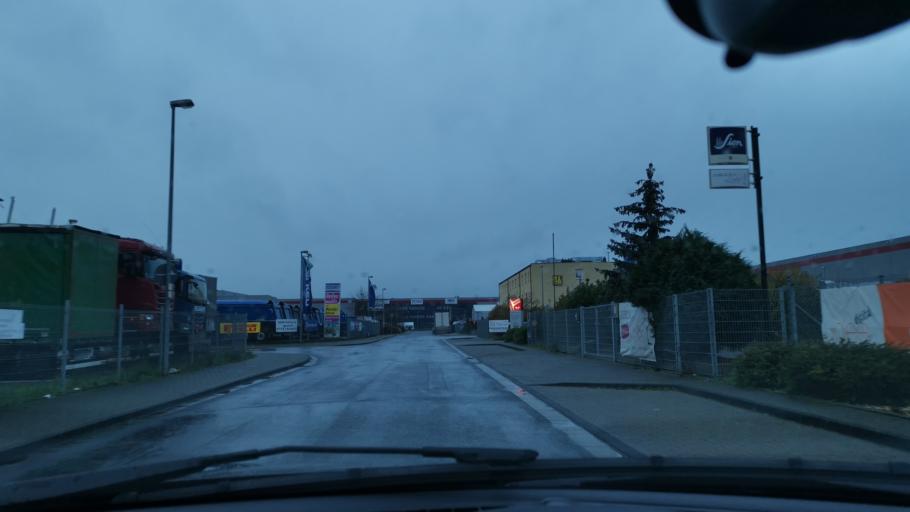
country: DE
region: North Rhine-Westphalia
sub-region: Regierungsbezirk Koln
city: Bedburg
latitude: 51.0135
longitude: 6.5766
